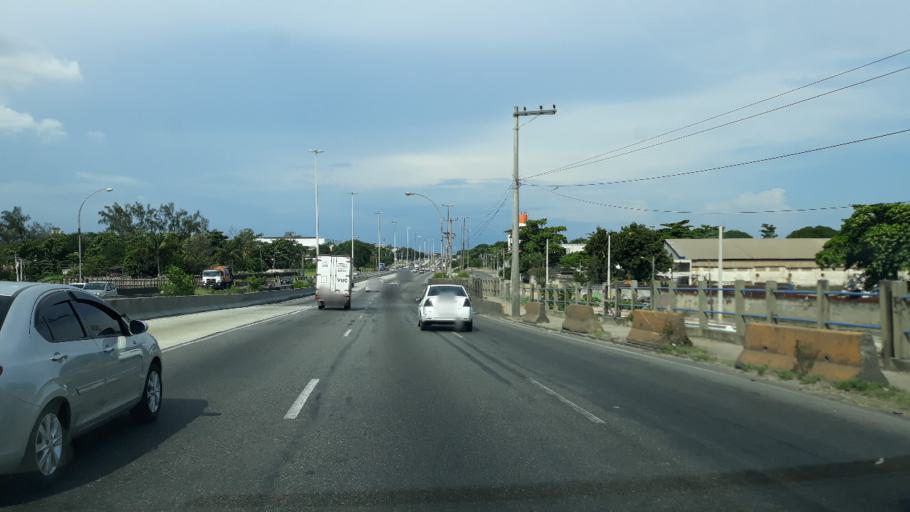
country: BR
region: Rio de Janeiro
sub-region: Sao Joao De Meriti
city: Sao Joao de Meriti
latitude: -22.8348
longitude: -43.3604
